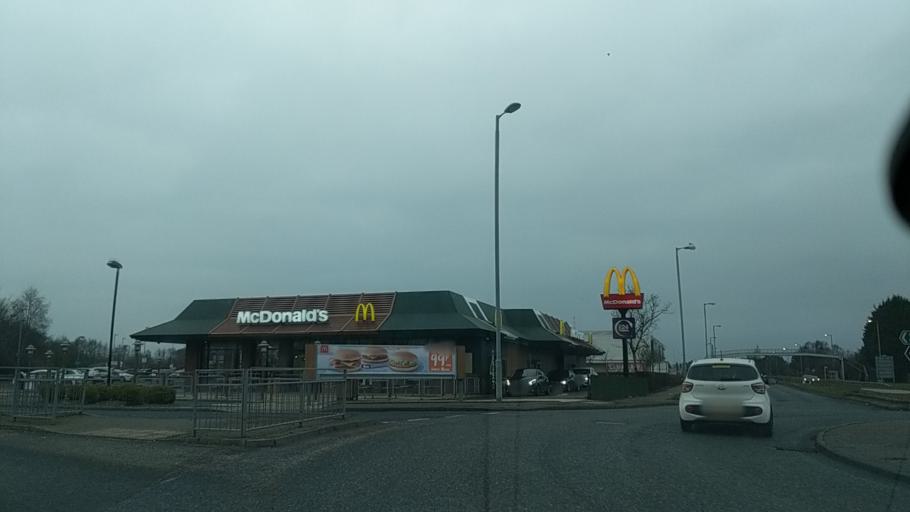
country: GB
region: Scotland
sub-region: South Lanarkshire
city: East Kilbride
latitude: 55.7649
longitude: -4.2093
